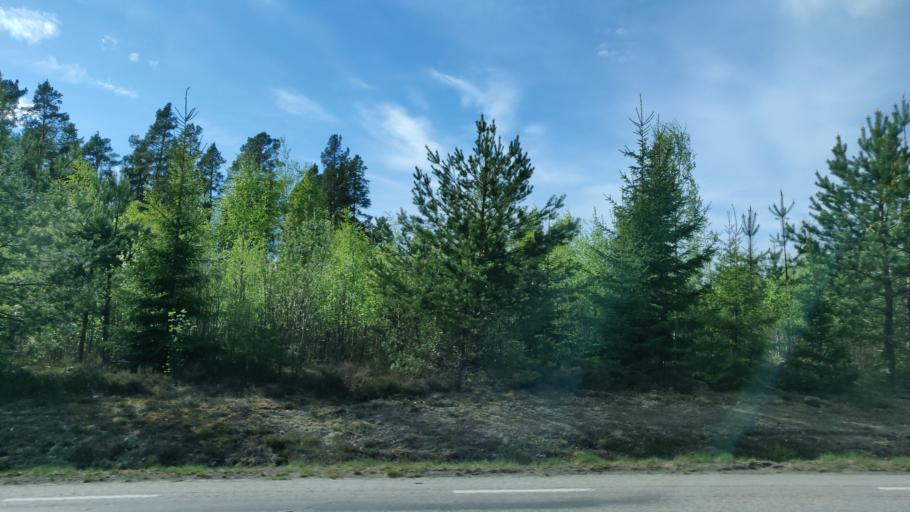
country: SE
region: Vaermland
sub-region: Forshaga Kommun
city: Forshaga
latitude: 59.4960
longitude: 13.4298
